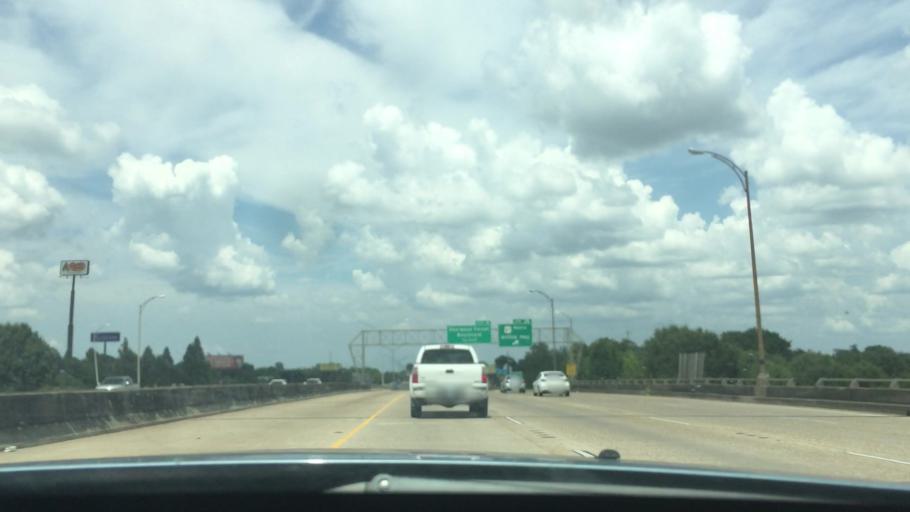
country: US
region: Louisiana
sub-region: East Baton Rouge Parish
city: Westminster
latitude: 30.4236
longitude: -91.0753
